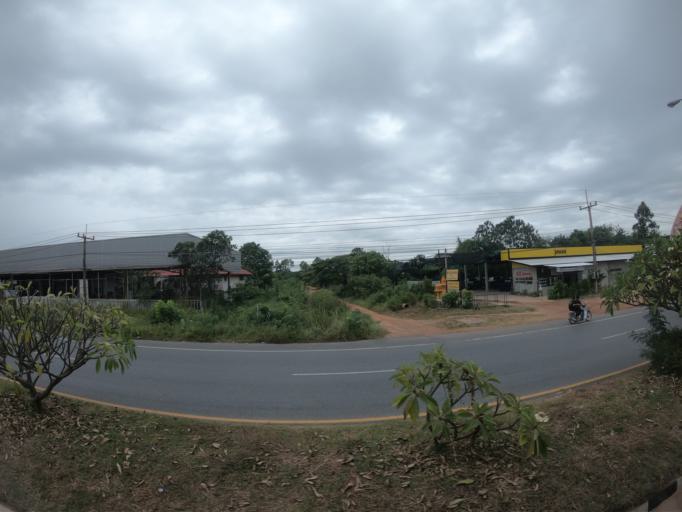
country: TH
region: Maha Sarakham
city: Maha Sarakham
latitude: 16.1677
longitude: 103.2885
